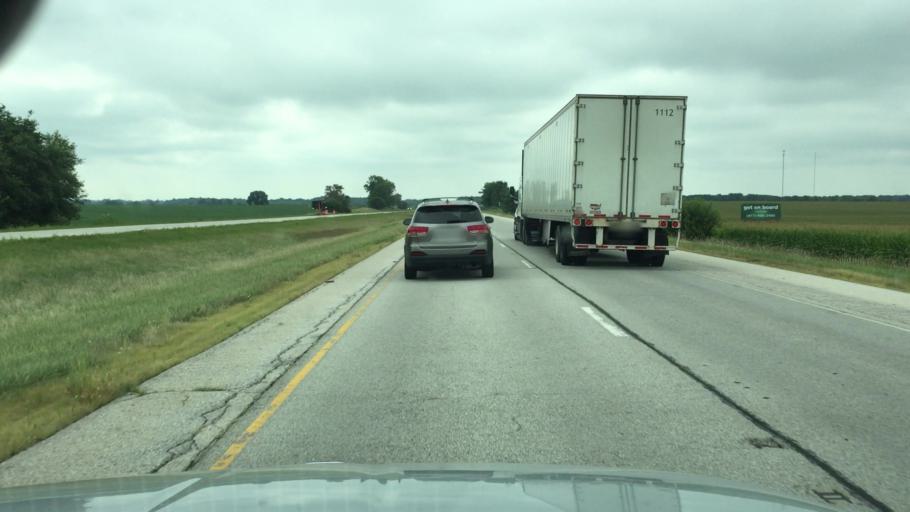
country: US
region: Illinois
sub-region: Knox County
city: Galesburg
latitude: 41.0942
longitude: -90.3332
